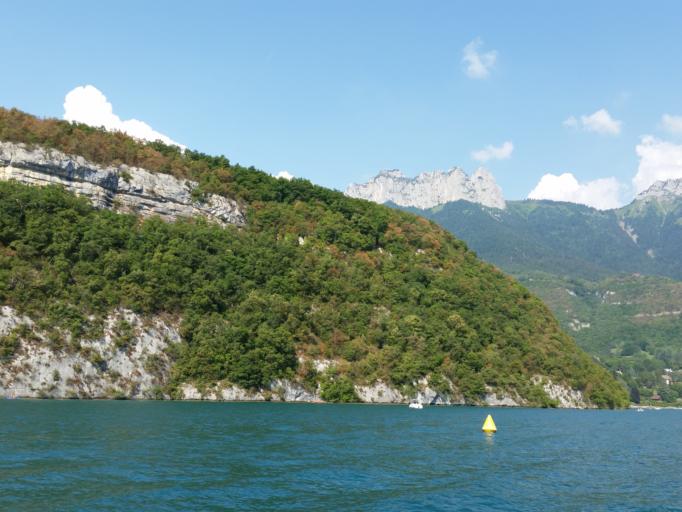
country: FR
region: Rhone-Alpes
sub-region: Departement de la Haute-Savoie
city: Talloires
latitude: 45.8392
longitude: 6.1963
